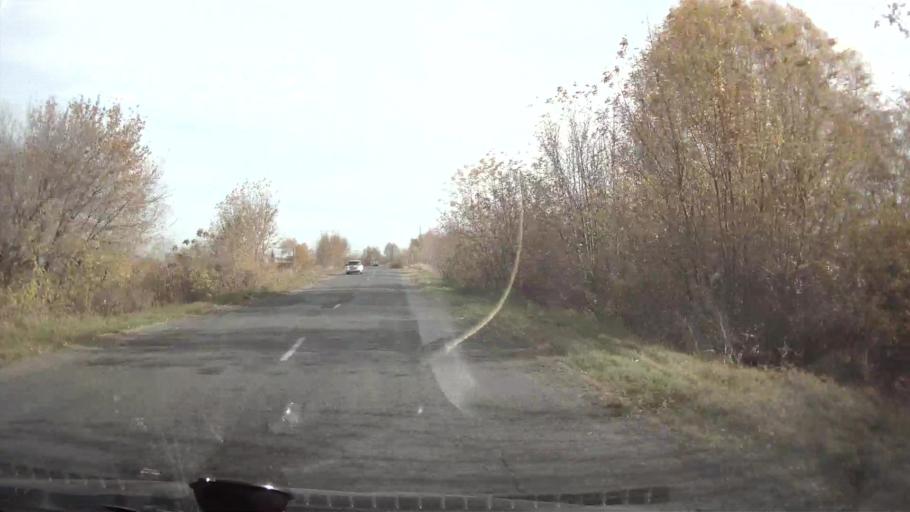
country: RU
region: Chuvashia
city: Alatyr'
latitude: 54.8439
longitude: 46.4695
